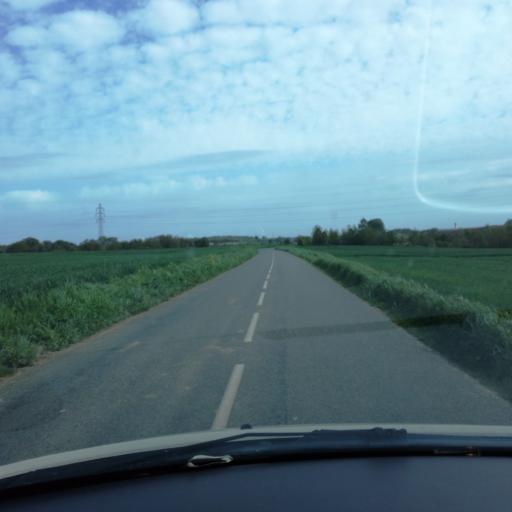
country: FR
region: Picardie
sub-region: Departement de la Somme
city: Poix-de-Picardie
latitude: 49.8028
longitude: 1.9995
